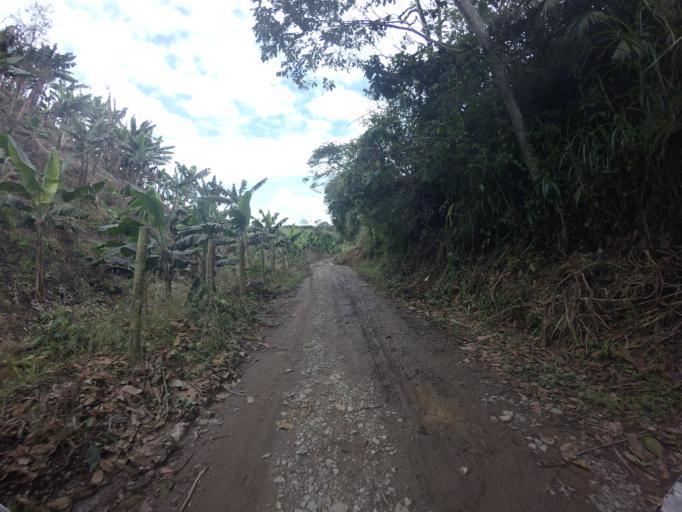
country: CO
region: Valle del Cauca
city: Ulloa
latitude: 4.6949
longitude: -75.7237
